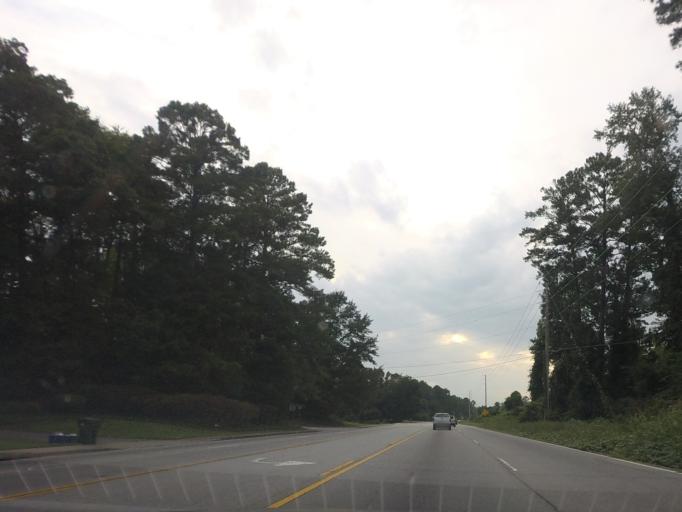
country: US
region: Georgia
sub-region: Bibb County
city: Macon
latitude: 32.8784
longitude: -83.7201
